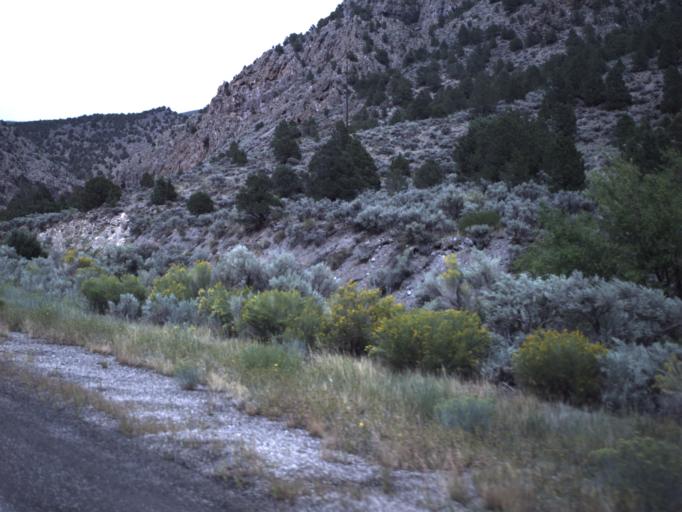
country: US
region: Utah
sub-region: Piute County
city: Junction
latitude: 38.1099
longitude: -112.3372
